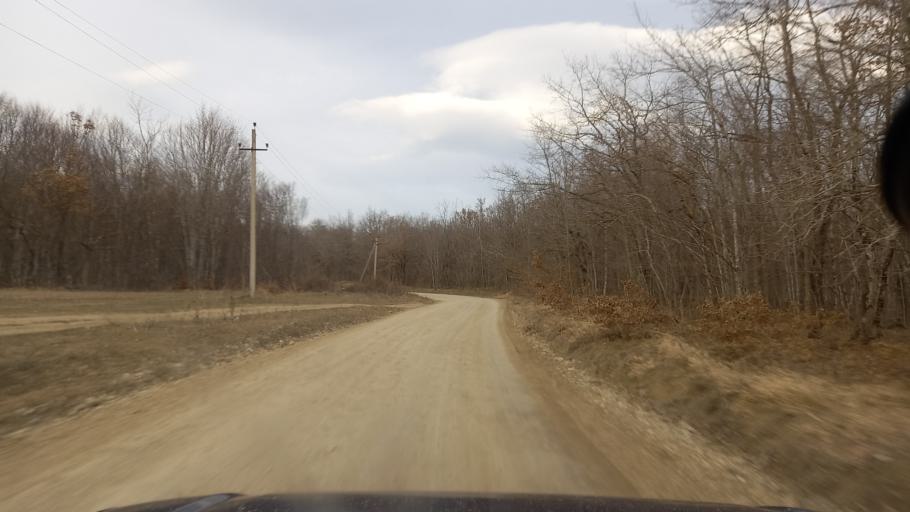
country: RU
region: Adygeya
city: Kamennomostskiy
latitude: 44.1435
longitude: 40.2578
